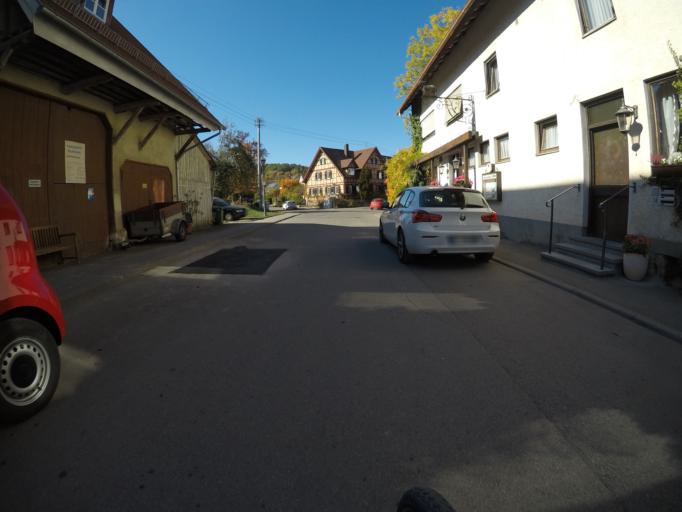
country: DE
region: Baden-Wuerttemberg
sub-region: Tuebingen Region
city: Rottenburg
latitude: 48.5264
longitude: 8.9599
